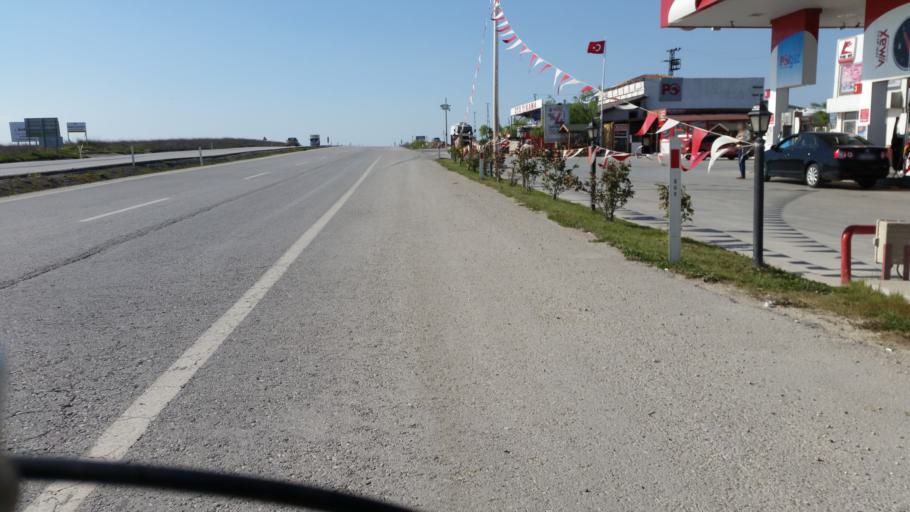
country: TR
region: Tekirdag
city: Cerkezkoey
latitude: 41.3408
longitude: 27.9652
